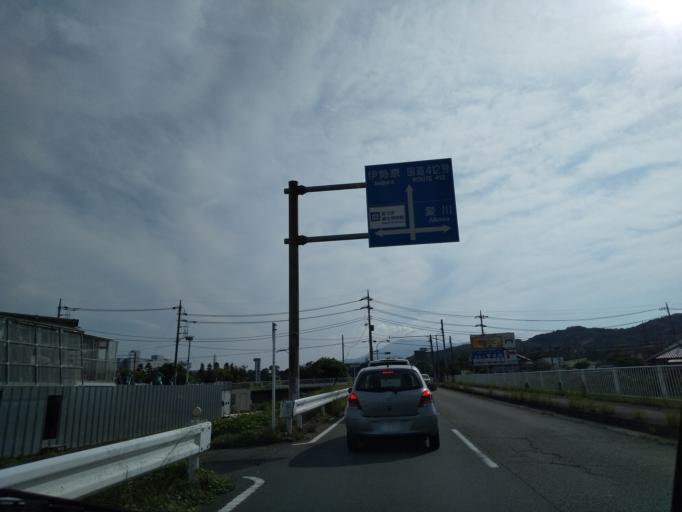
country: JP
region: Kanagawa
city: Zama
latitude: 35.4984
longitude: 139.3469
